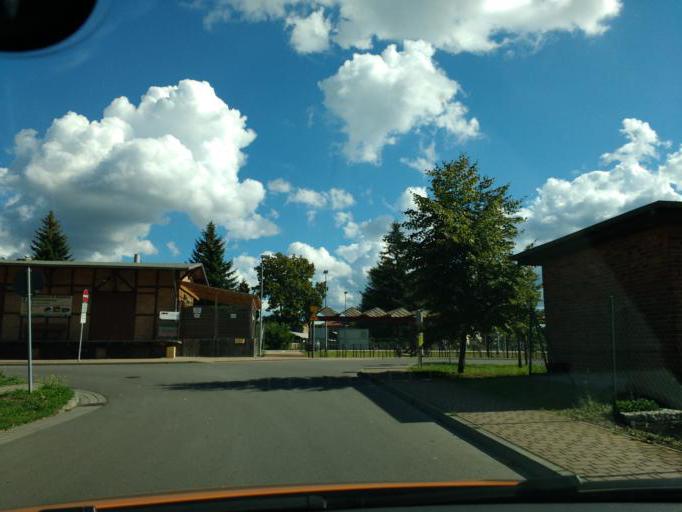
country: DE
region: Brandenburg
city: Bestensee
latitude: 52.2419
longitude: 13.6342
